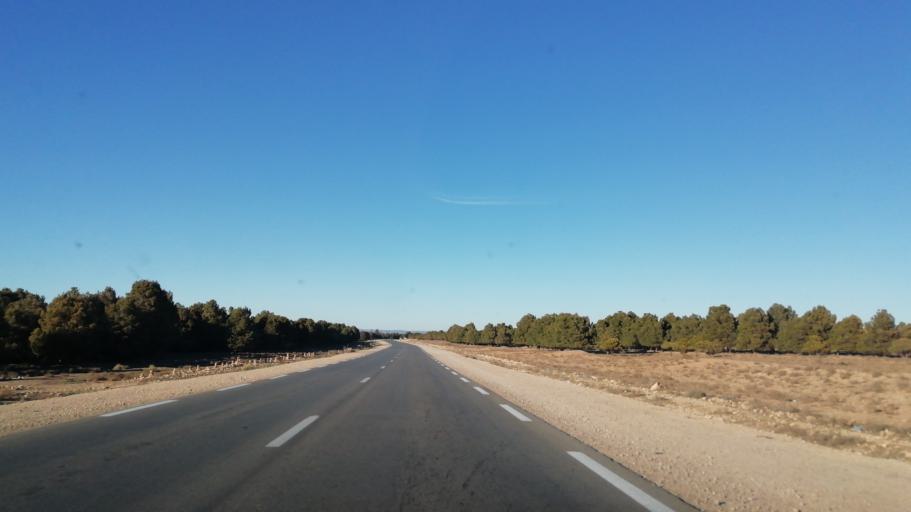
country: DZ
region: Tlemcen
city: Sebdou
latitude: 34.4530
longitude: -1.2753
